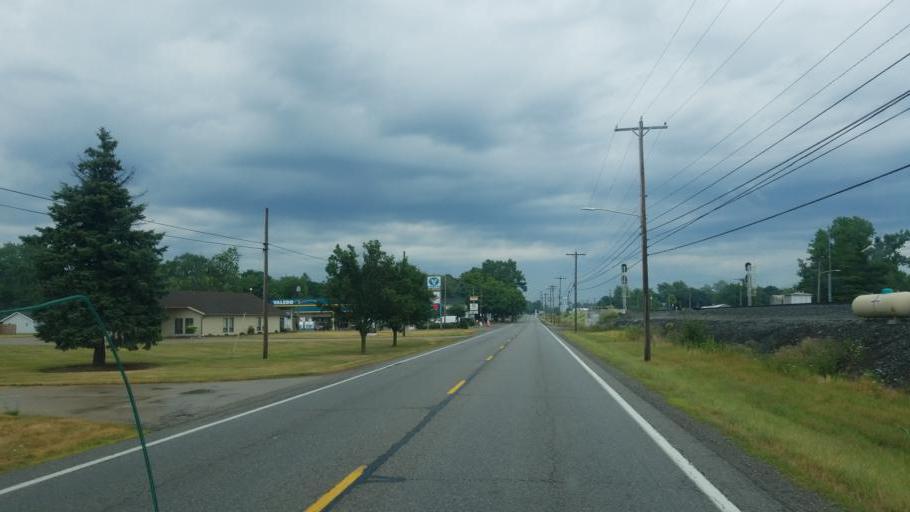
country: US
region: Ohio
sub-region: Williams County
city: Edgerton
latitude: 41.4468
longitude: -84.7551
